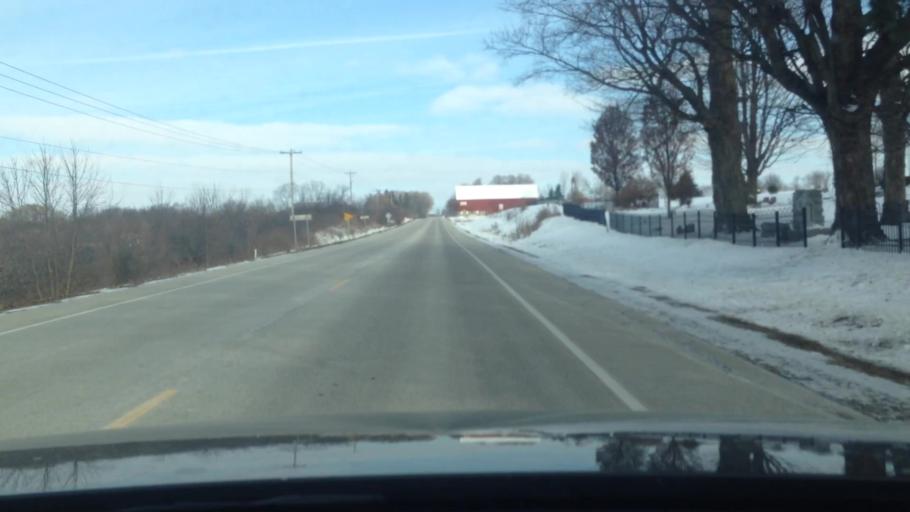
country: US
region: Wisconsin
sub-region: Walworth County
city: Lake Geneva
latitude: 42.6551
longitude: -88.4136
